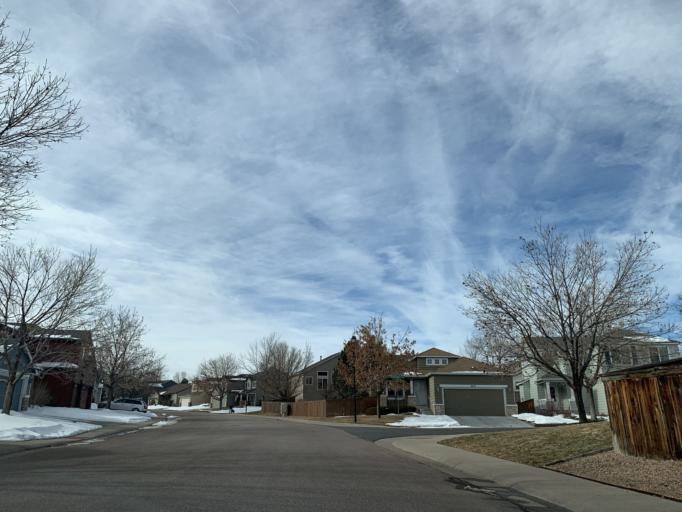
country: US
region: Colorado
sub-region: Douglas County
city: Carriage Club
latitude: 39.5413
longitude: -104.9256
